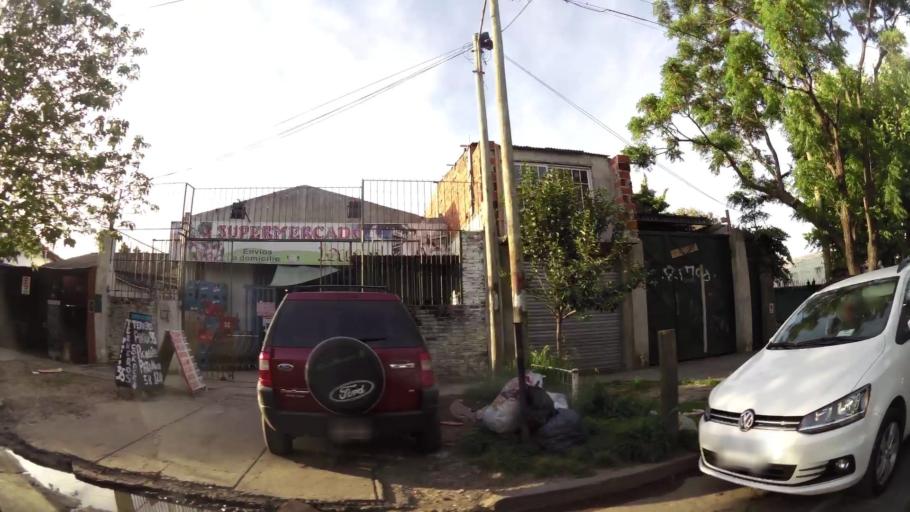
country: AR
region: Buenos Aires
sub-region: Partido de Almirante Brown
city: Adrogue
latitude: -34.7944
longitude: -58.3513
